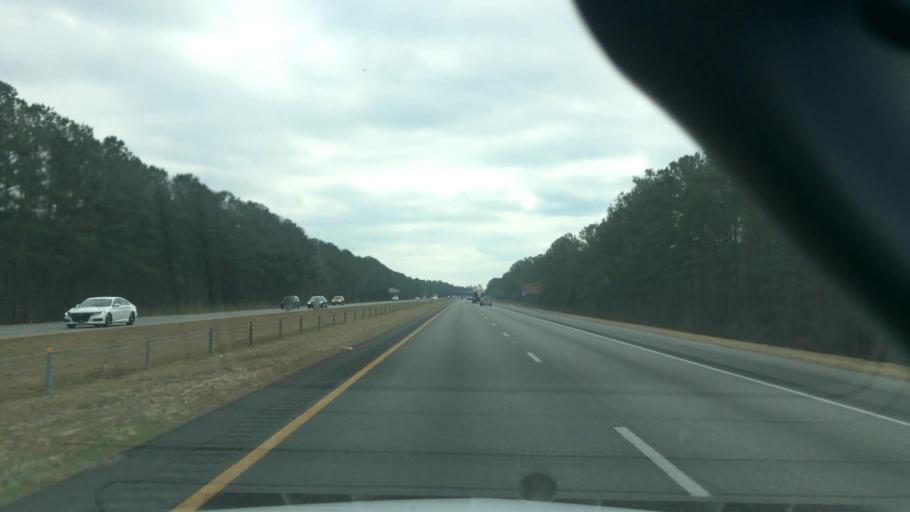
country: US
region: North Carolina
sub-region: New Hanover County
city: Skippers Corner
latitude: 34.3369
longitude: -77.8775
